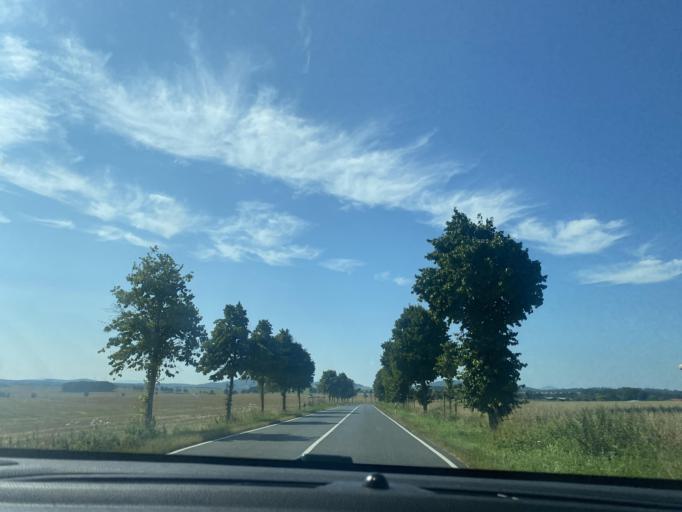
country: DE
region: Saxony
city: Bernstadt
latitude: 51.0312
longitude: 14.8113
